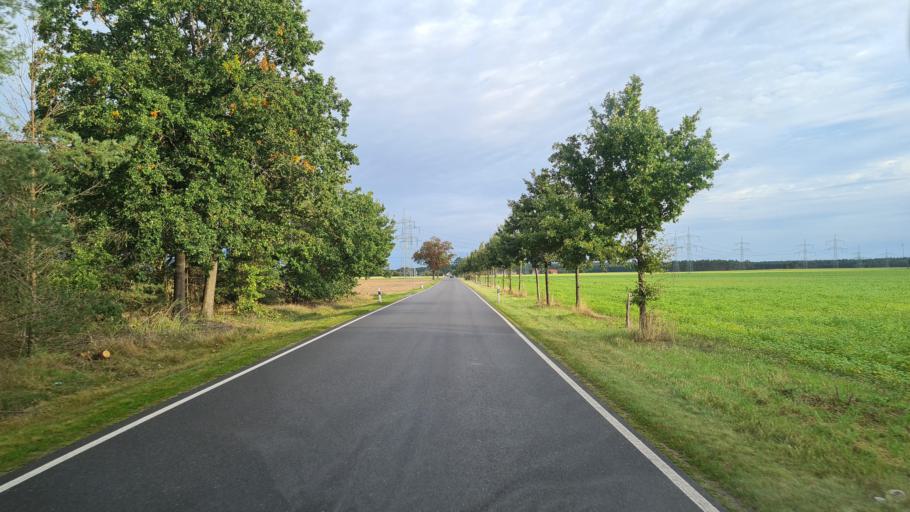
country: DE
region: Brandenburg
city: Luckau
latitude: 51.8907
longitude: 13.7153
